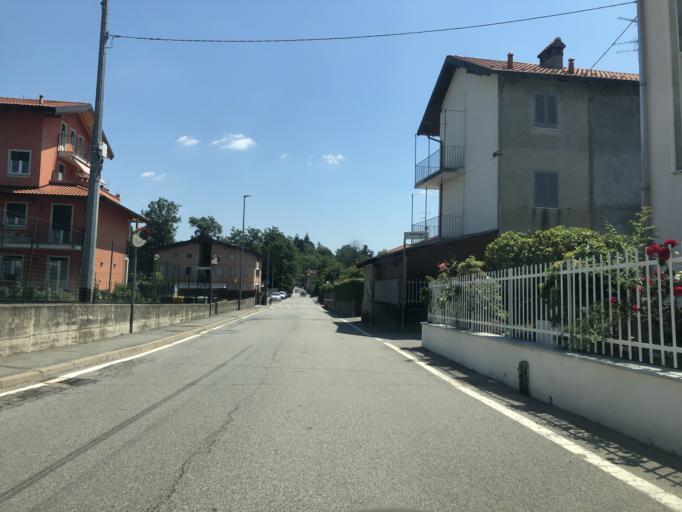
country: IT
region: Piedmont
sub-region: Provincia di Novara
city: Oleggio Castello
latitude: 45.7518
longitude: 8.5265
